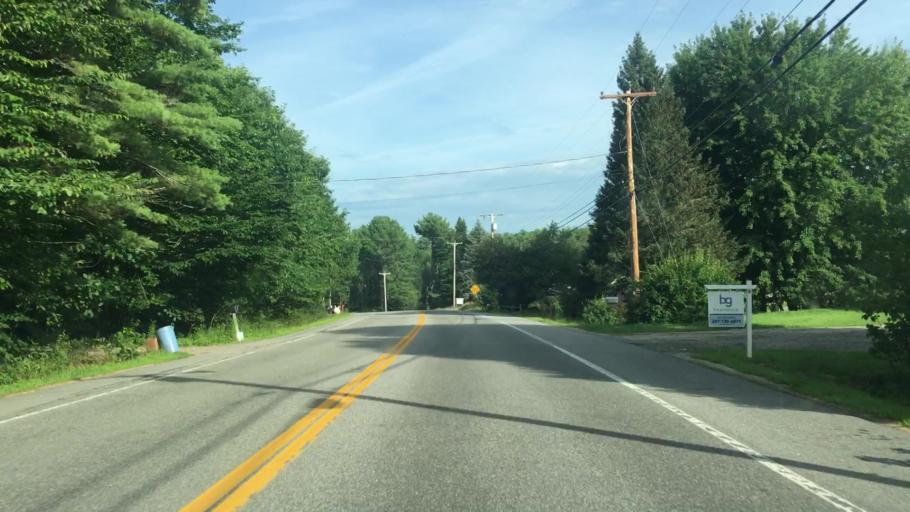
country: US
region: Maine
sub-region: York County
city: Limington
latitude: 43.7370
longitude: -70.6676
